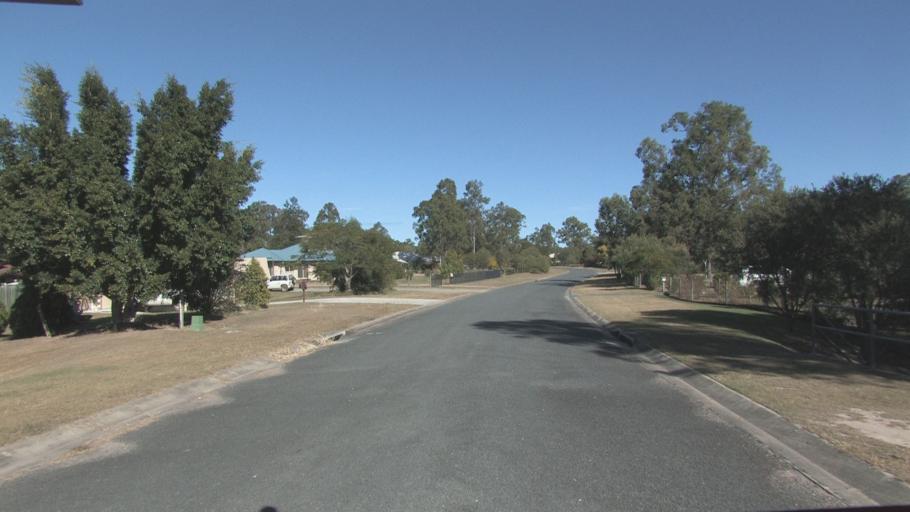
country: AU
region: Queensland
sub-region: Logan
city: North Maclean
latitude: -27.8171
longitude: 152.9529
